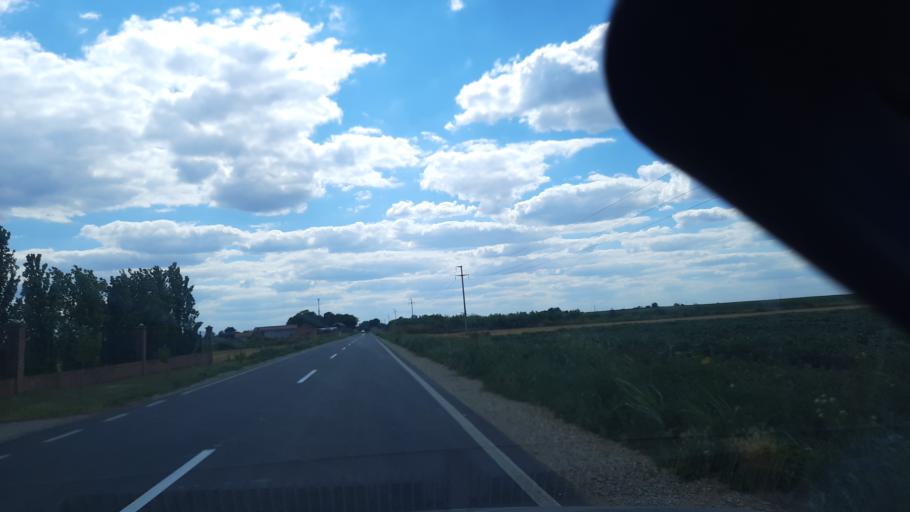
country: RS
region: Autonomna Pokrajina Vojvodina
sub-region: Sremski Okrug
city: Pecinci
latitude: 44.9213
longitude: 19.9804
